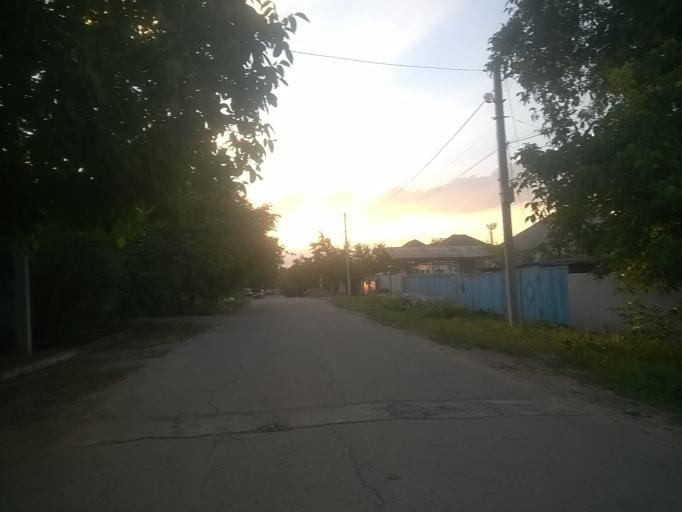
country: RU
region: Rostov
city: Donetsk
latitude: 48.3354
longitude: 39.9549
